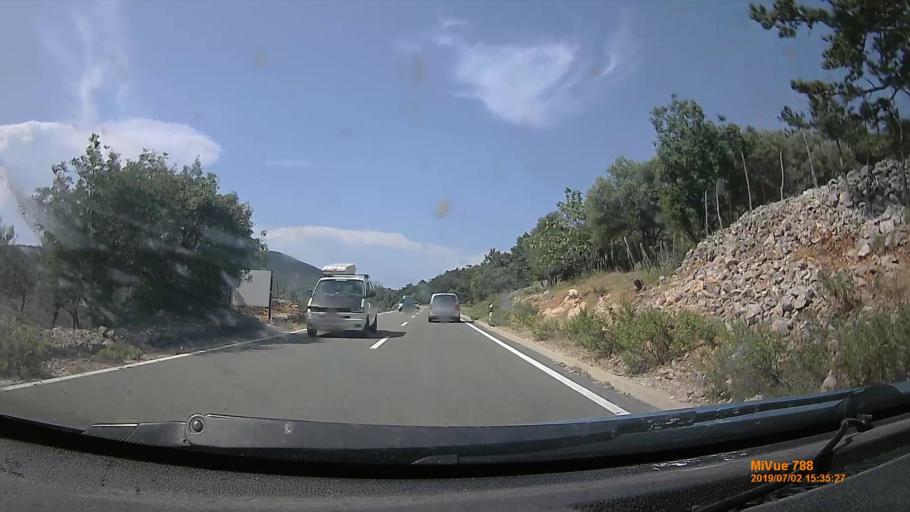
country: HR
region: Primorsko-Goranska
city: Cres
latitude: 44.9762
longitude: 14.4123
